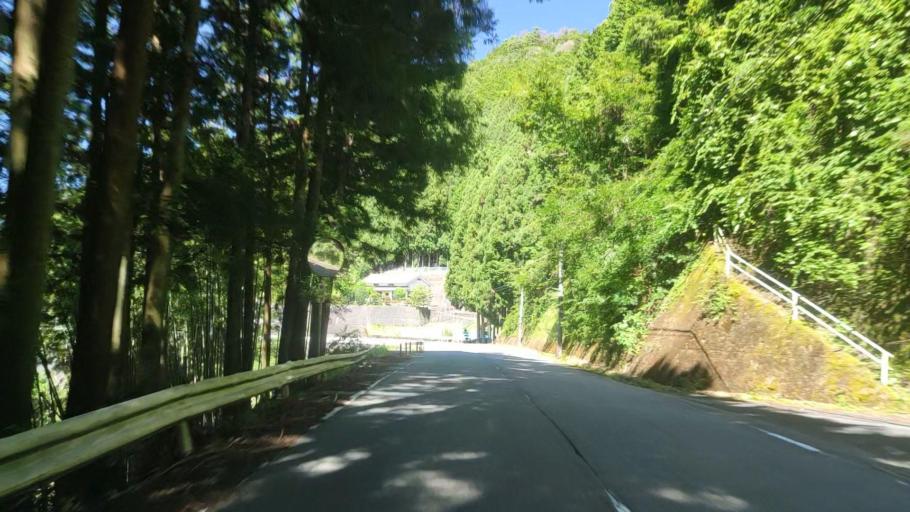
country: JP
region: Nara
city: Yoshino-cho
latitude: 34.3989
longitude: 135.9261
